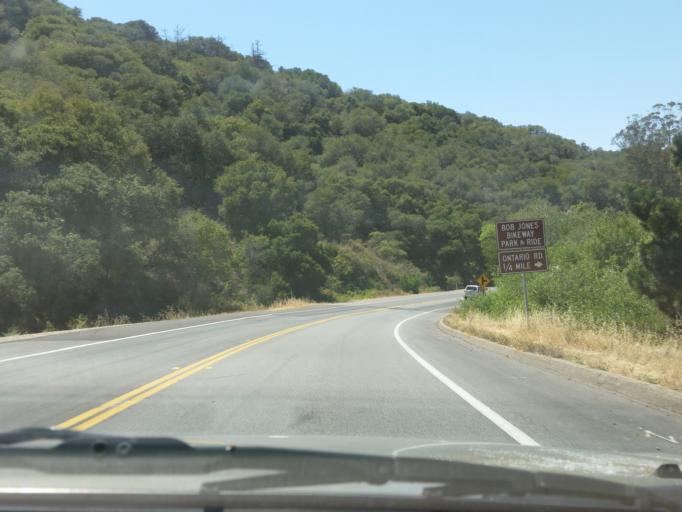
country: US
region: California
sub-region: San Luis Obispo County
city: Avila Beach
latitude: 35.1798
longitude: -120.7018
